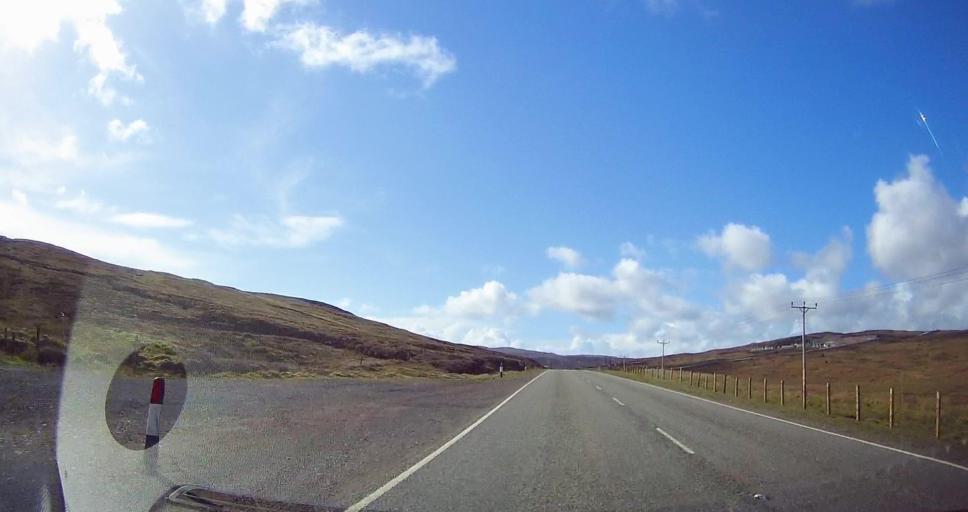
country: GB
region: Scotland
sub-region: Shetland Islands
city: Lerwick
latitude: 60.2695
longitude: -1.2338
